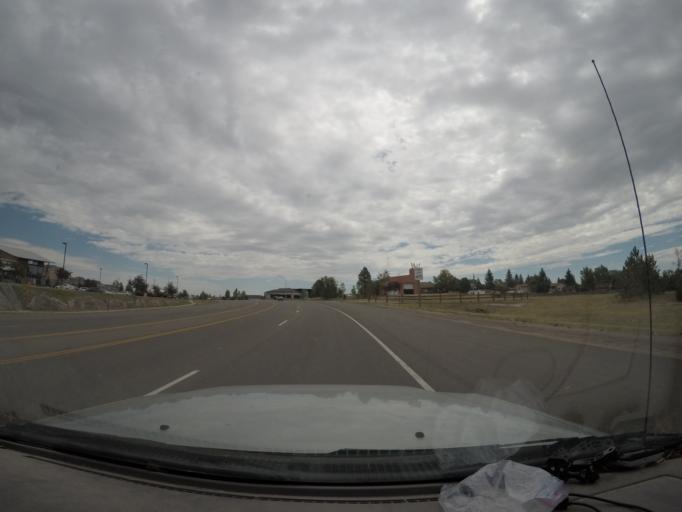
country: US
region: Wyoming
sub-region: Laramie County
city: Fox Farm-College
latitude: 41.1419
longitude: -104.7592
